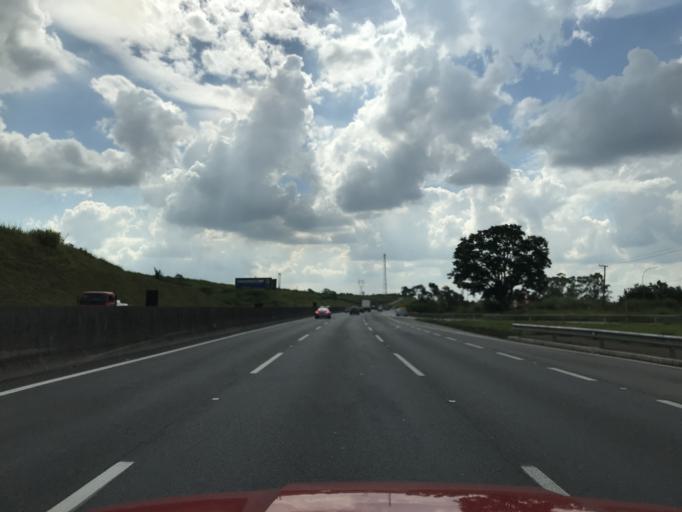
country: BR
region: Sao Paulo
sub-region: Louveira
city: Louveira
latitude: -23.1296
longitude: -46.9510
